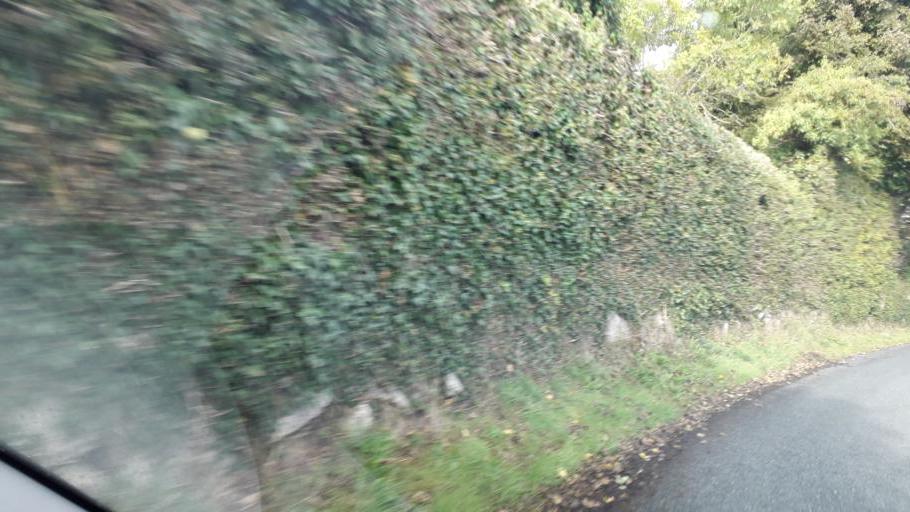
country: IE
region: Leinster
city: Sandyford
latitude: 53.2499
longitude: -6.2146
